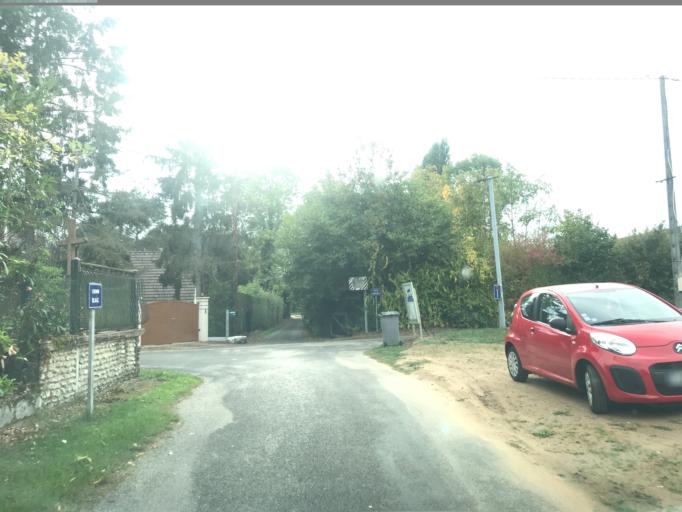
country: FR
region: Haute-Normandie
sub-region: Departement de l'Eure
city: Heudreville-sur-Eure
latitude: 49.1346
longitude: 1.2062
